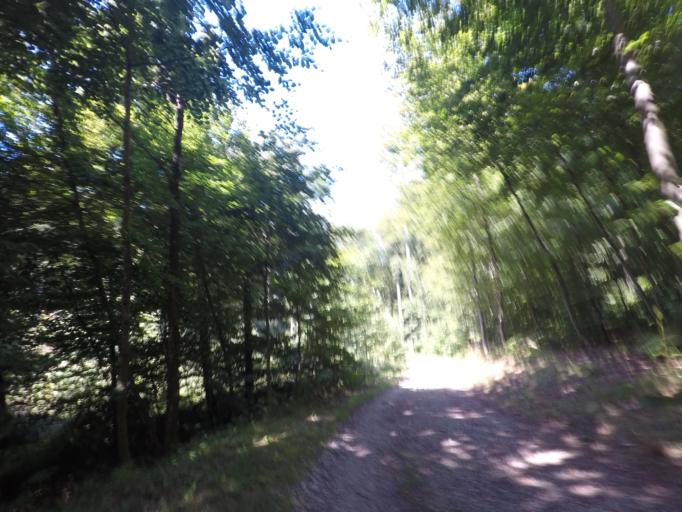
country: LU
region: Luxembourg
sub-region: Canton de Luxembourg
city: Strassen
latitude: 49.6381
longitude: 6.0748
